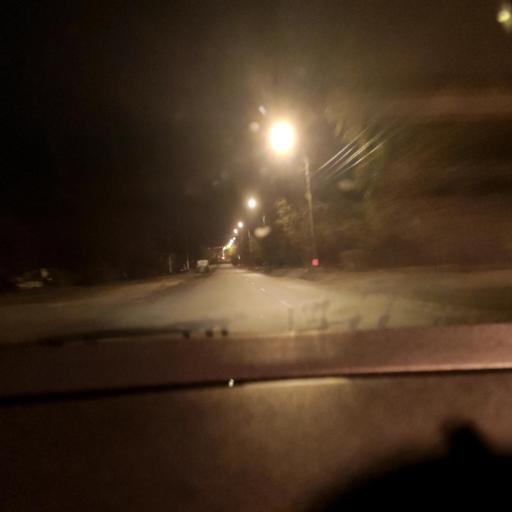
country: RU
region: Voronezj
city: Voronezh
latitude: 51.6977
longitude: 39.1713
